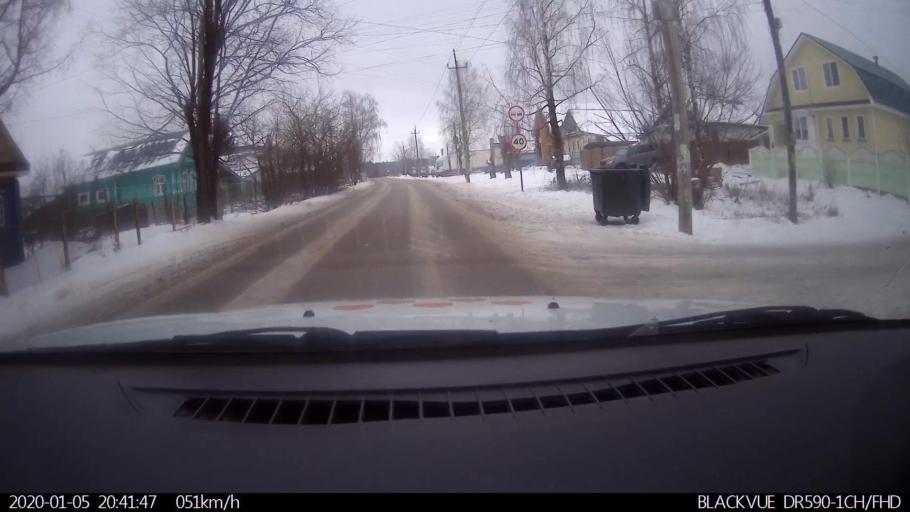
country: RU
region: Nizjnij Novgorod
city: Lukino
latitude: 56.4008
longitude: 43.7294
